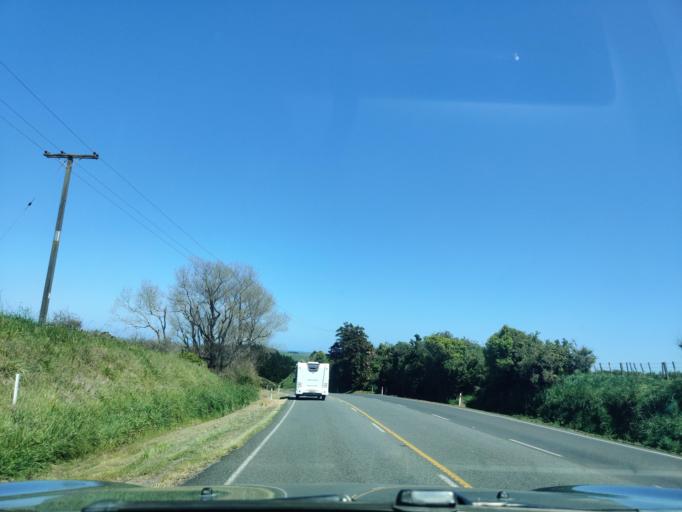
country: NZ
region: Taranaki
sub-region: South Taranaki District
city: Patea
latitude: -39.8097
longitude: 174.7479
